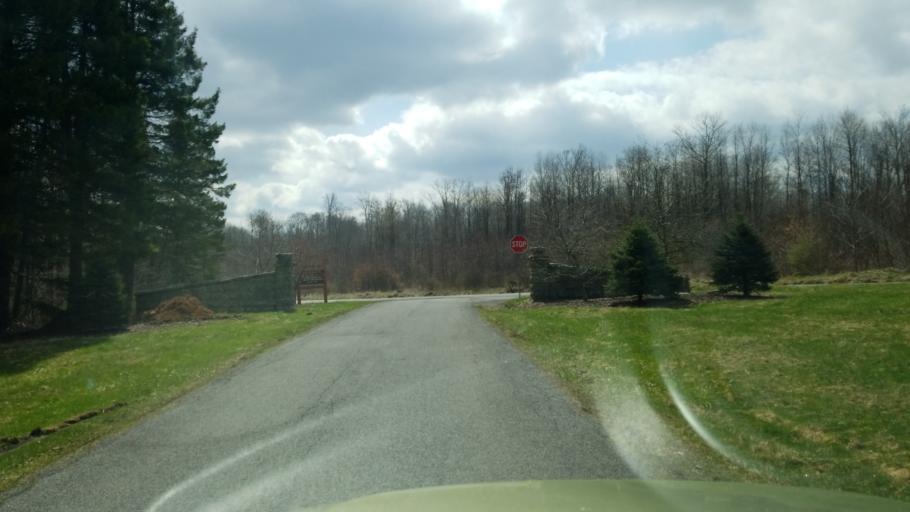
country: US
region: Pennsylvania
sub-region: Jefferson County
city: Brockway
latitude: 41.2802
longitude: -78.8692
